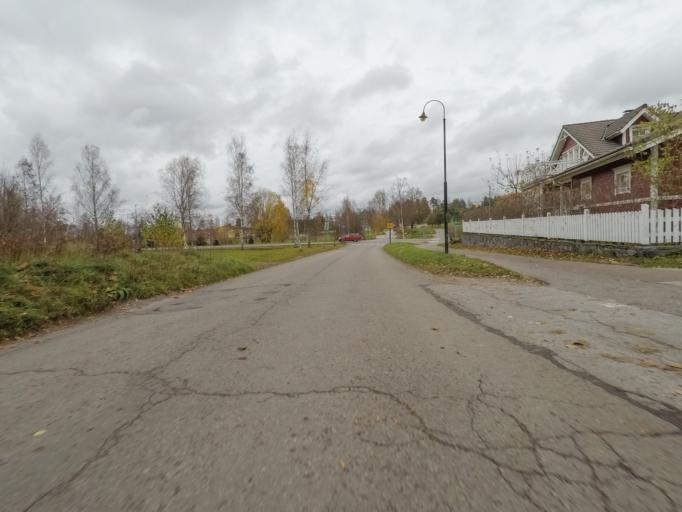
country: FI
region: Uusimaa
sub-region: Porvoo
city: Porvoo
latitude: 60.4053
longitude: 25.6649
